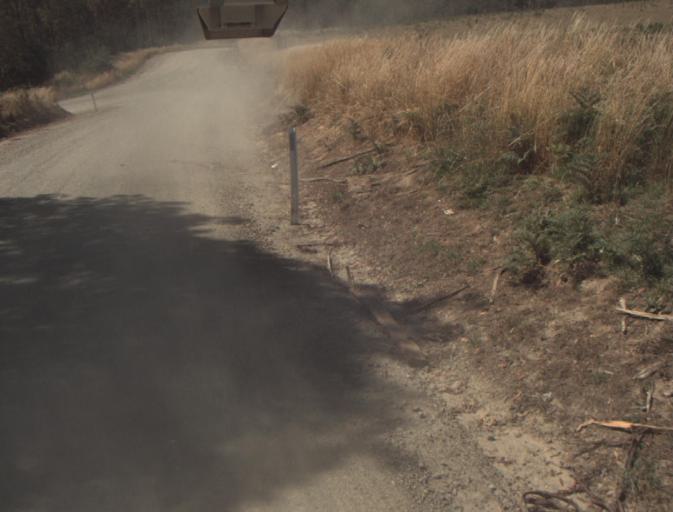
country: AU
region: Tasmania
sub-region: Dorset
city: Scottsdale
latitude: -41.3314
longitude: 147.4360
